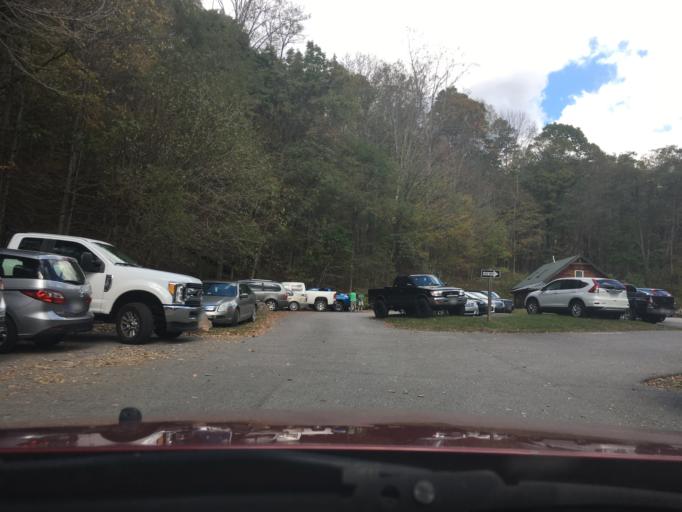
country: US
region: Virginia
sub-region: Giles County
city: Pembroke
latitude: 37.3534
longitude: -80.5997
